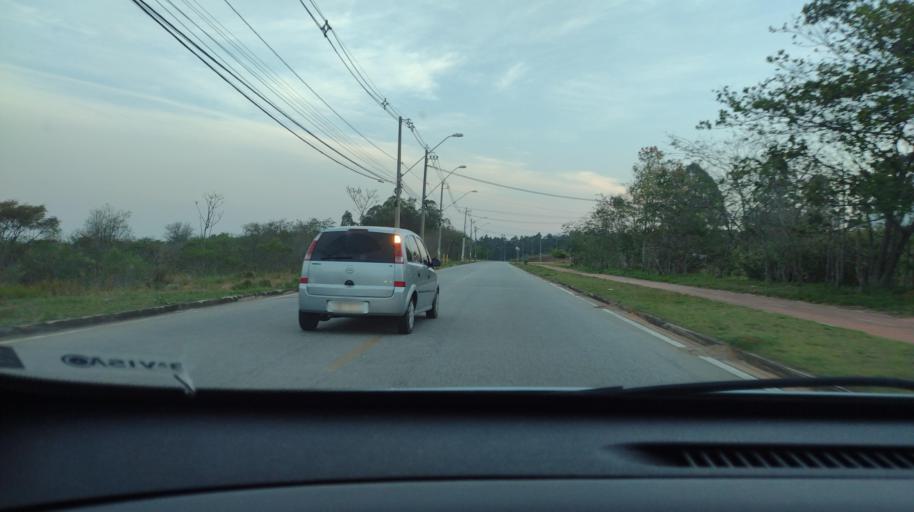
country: BR
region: Sao Paulo
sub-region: Sorocaba
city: Sorocaba
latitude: -23.3724
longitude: -47.4736
